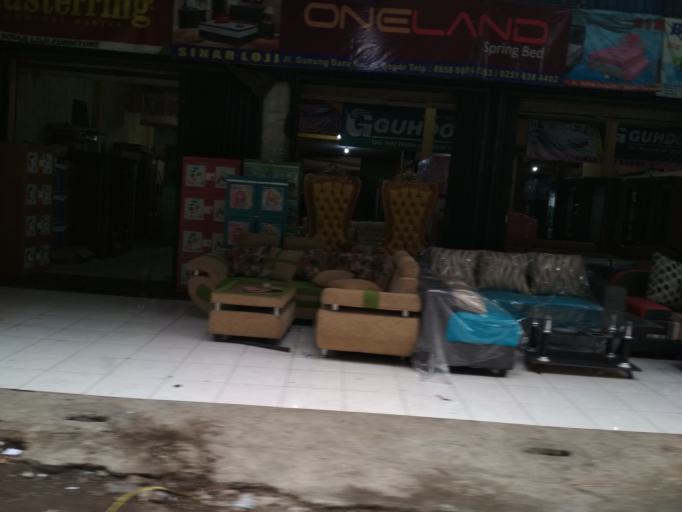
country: ID
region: West Java
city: Bogor
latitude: -6.5891
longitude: 106.7733
